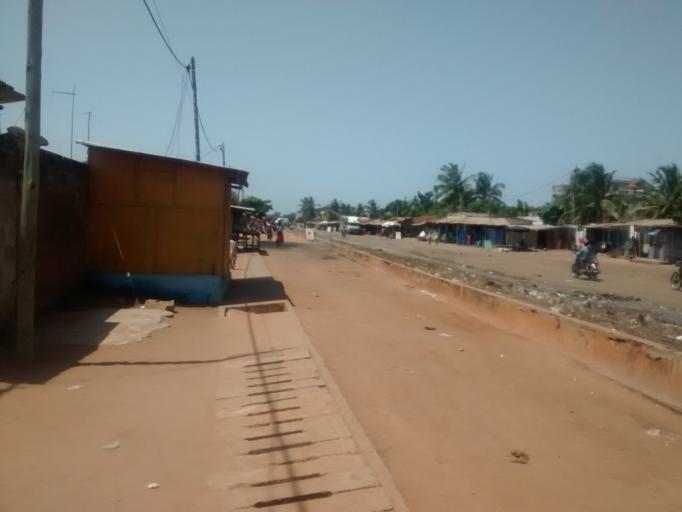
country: TG
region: Maritime
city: Lome
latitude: 6.1533
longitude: 1.2485
